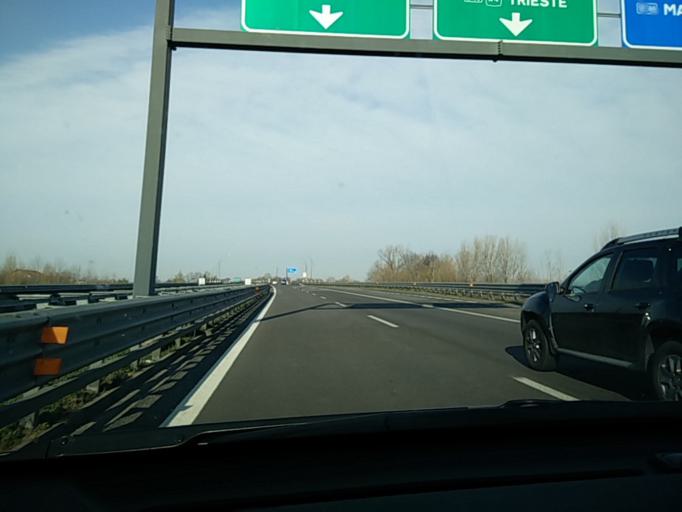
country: IT
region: Veneto
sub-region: Provincia di Venezia
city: Dese
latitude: 45.5332
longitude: 12.3093
